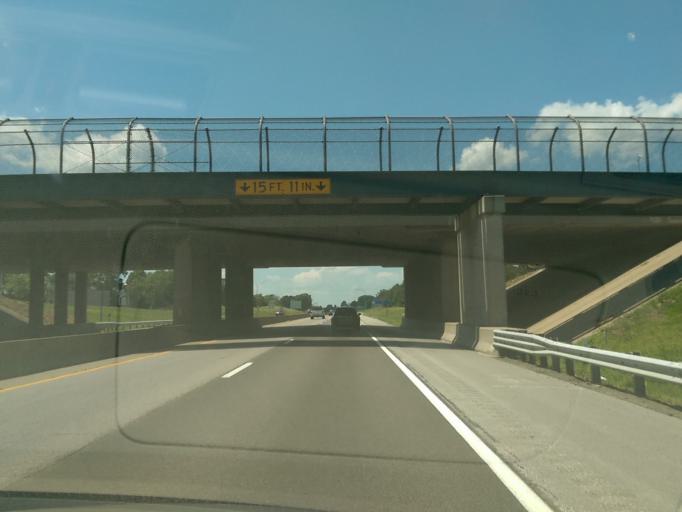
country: US
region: Missouri
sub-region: Boone County
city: Columbia
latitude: 38.9691
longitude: -92.3332
